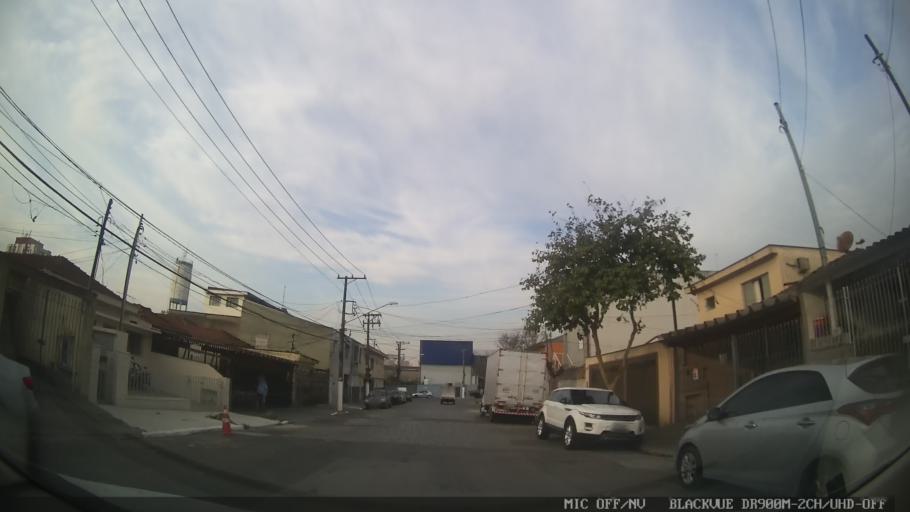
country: BR
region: Sao Paulo
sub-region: Sao Caetano Do Sul
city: Sao Caetano do Sul
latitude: -23.6034
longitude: -46.5859
